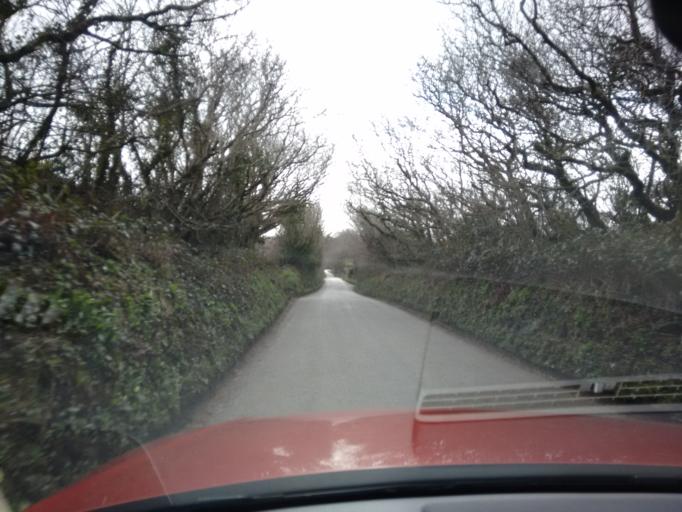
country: GB
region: England
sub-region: Cornwall
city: Liskeard
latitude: 50.4786
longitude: -4.5159
